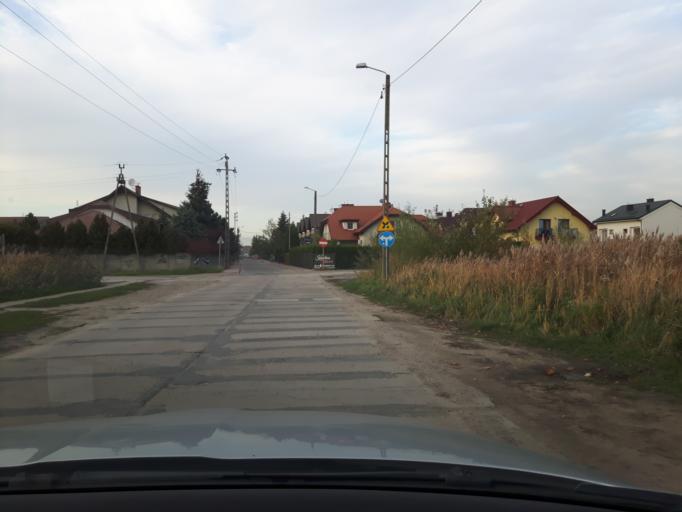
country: PL
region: Masovian Voivodeship
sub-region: Powiat wolominski
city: Zabki
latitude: 52.2807
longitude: 21.1188
